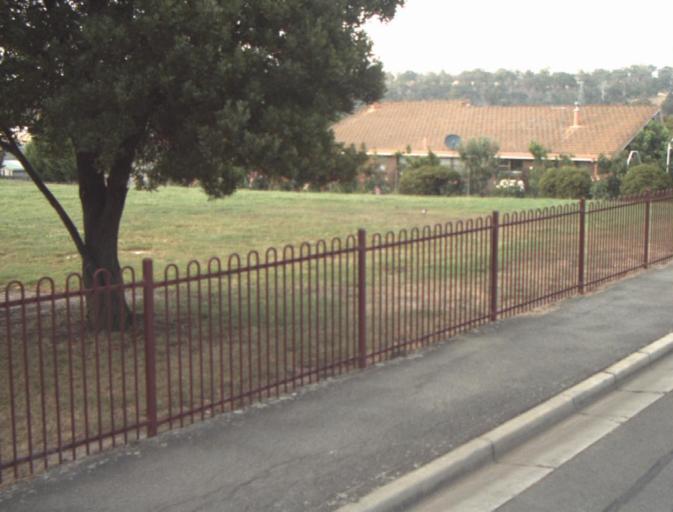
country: AU
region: Tasmania
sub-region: Launceston
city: Summerhill
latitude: -41.4827
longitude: 147.1627
